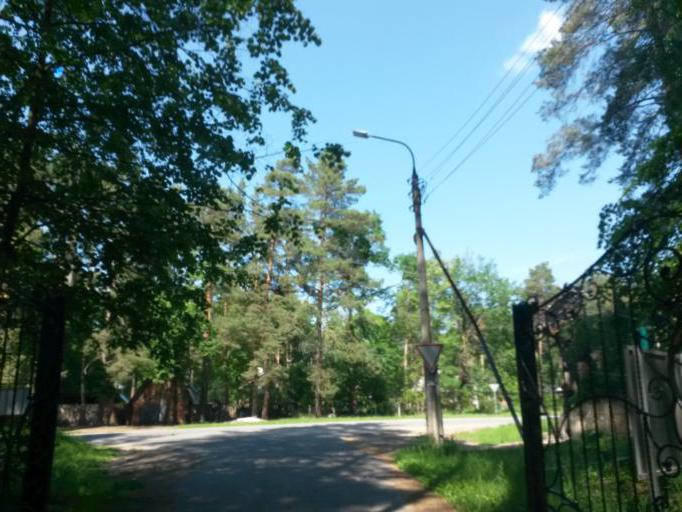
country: RU
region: Moskovskaya
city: Danki
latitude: 54.9119
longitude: 37.5731
